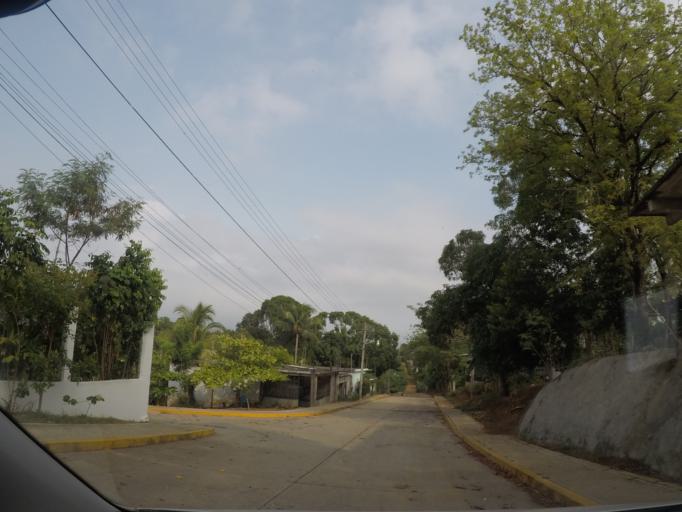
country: MX
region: Oaxaca
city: Colonia Rincon Viejo
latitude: 16.8873
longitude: -95.0468
